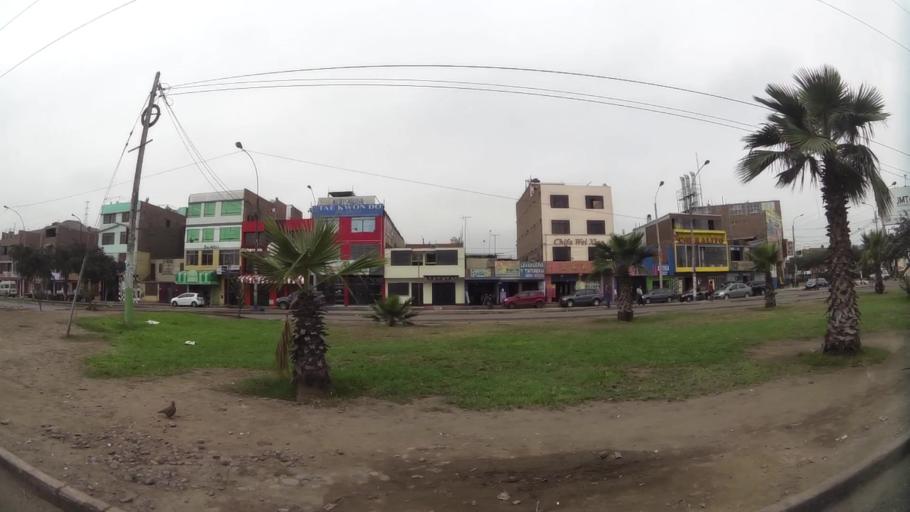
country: PE
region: Lima
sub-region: Lima
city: Independencia
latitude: -12.0060
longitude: -77.0827
